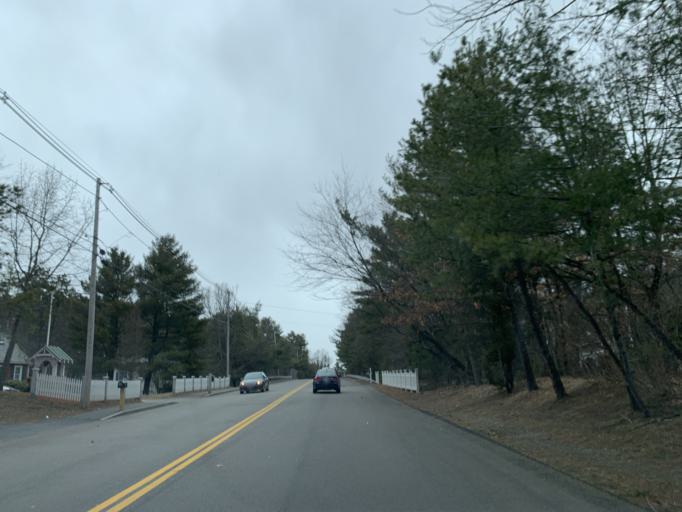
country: US
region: Massachusetts
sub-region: Norfolk County
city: Franklin
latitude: 42.0968
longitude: -71.3735
